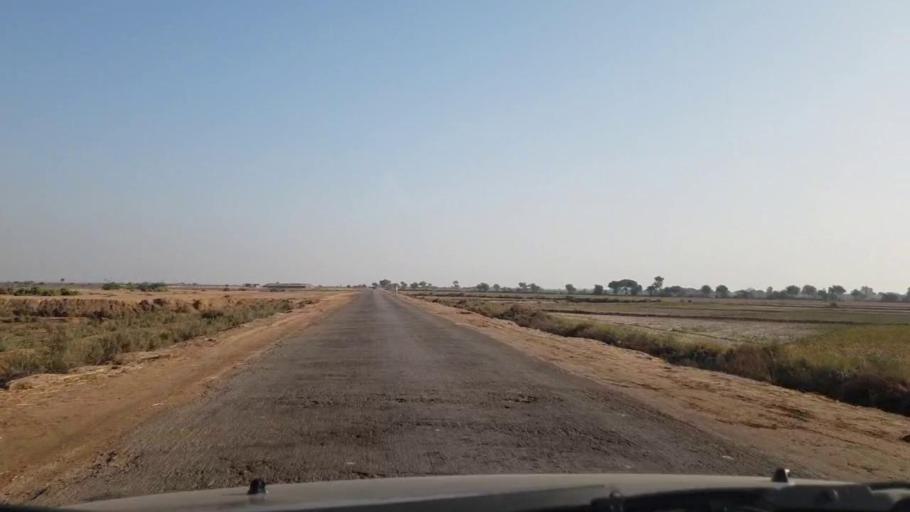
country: PK
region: Sindh
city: Tando Bago
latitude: 24.8165
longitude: 69.0015
